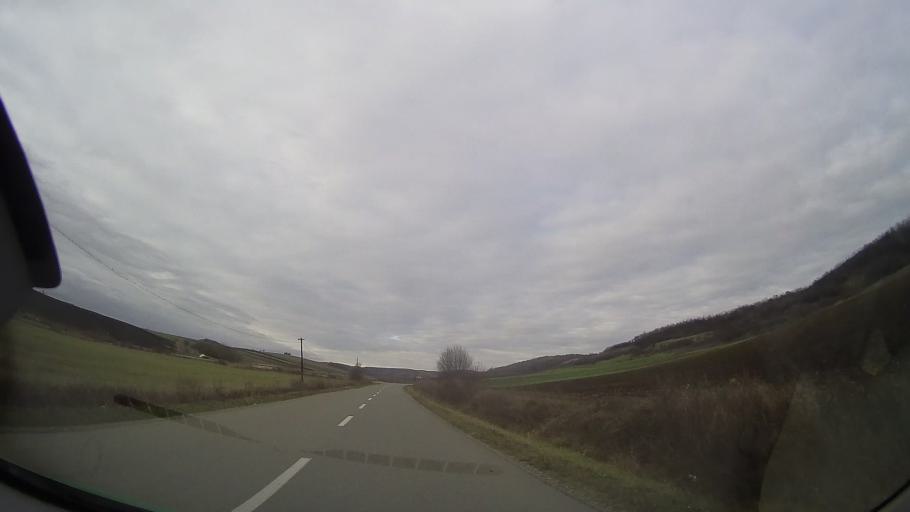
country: RO
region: Bistrita-Nasaud
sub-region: Comuna Milas
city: Milas
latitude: 46.7997
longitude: 24.4212
